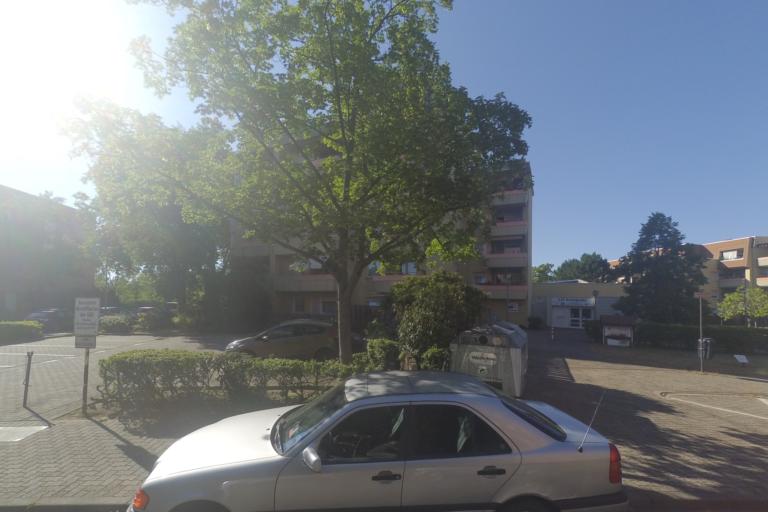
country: DE
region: Rheinland-Pfalz
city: Ludwigshafen am Rhein
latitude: 49.4803
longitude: 8.4375
